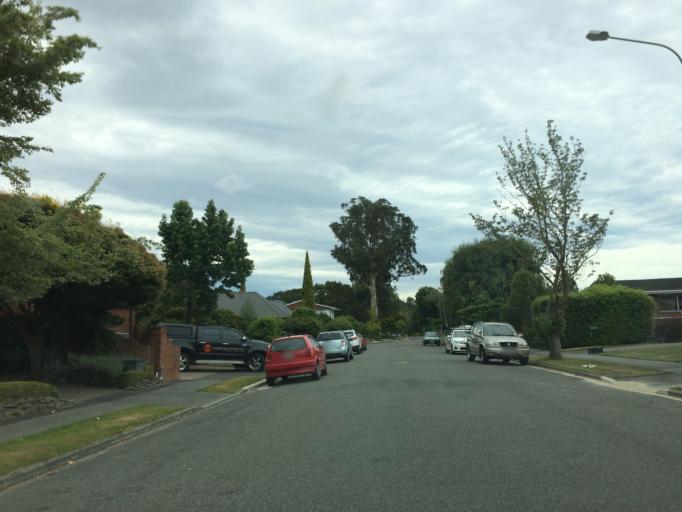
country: NZ
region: Canterbury
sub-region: Selwyn District
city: Prebbleton
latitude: -43.5209
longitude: 172.5469
